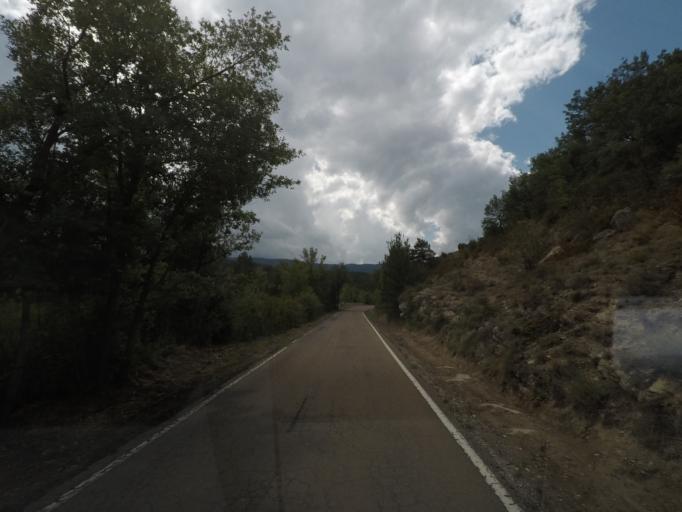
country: ES
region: Aragon
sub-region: Provincia de Huesca
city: Yebra de Basa
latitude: 42.3921
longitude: -0.2709
